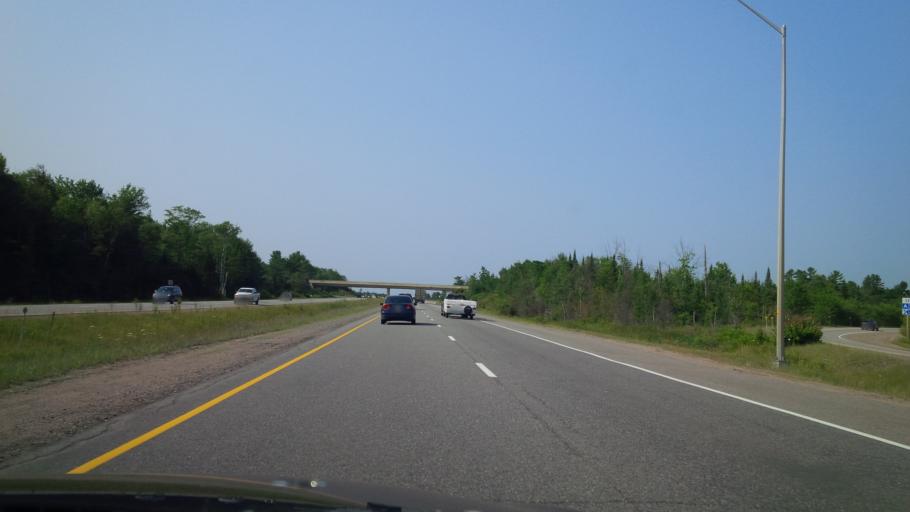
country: CA
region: Ontario
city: Bracebridge
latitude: 44.9987
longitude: -79.3045
